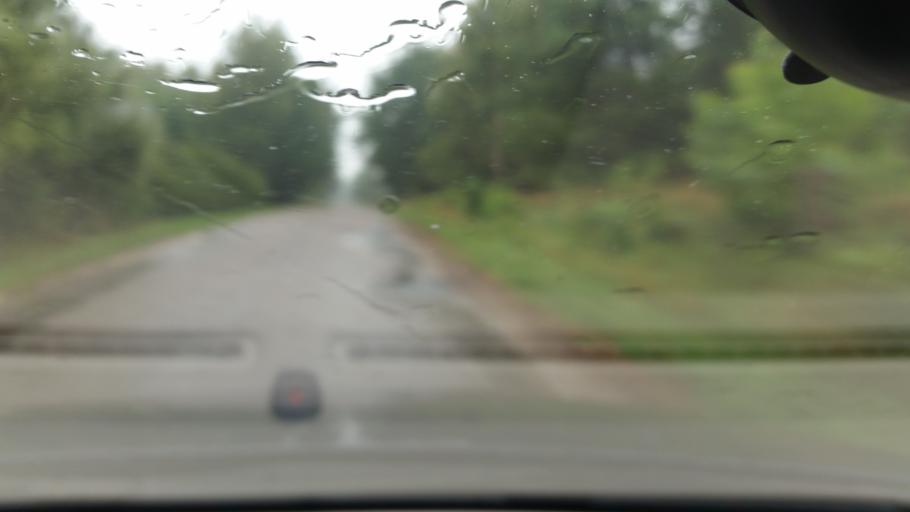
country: PL
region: Pomeranian Voivodeship
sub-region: Powiat wejherowski
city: Choczewo
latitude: 54.7634
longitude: 17.7928
